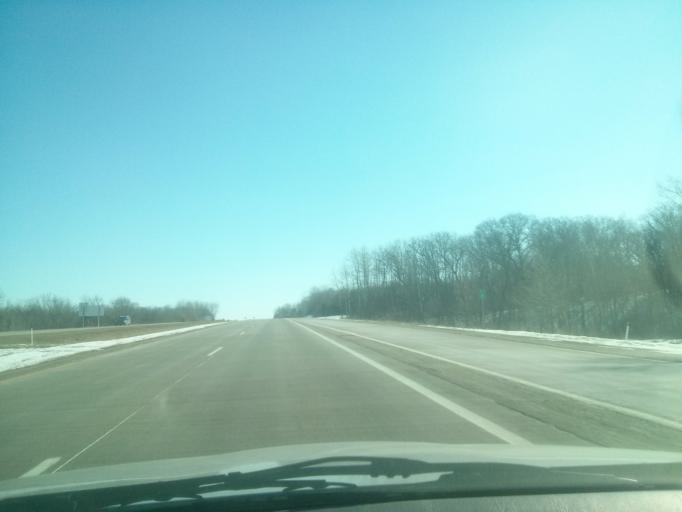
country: US
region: Wisconsin
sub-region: Saint Croix County
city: Somerset
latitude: 45.1070
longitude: -92.7197
